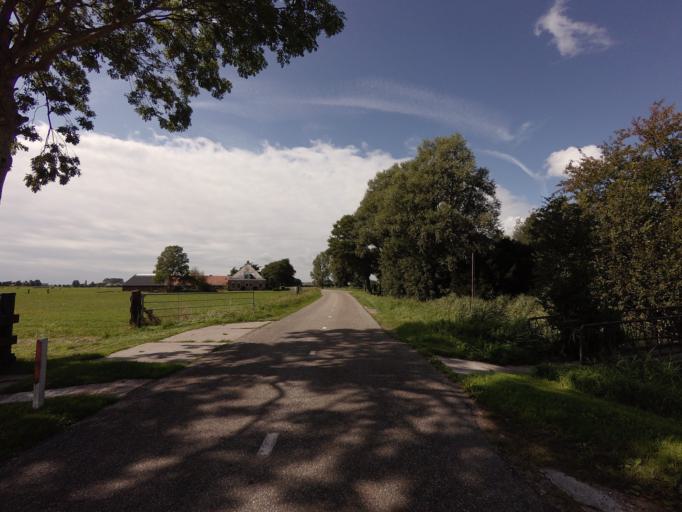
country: NL
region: Friesland
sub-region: Sudwest Fryslan
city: IJlst
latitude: 53.0270
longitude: 5.5816
